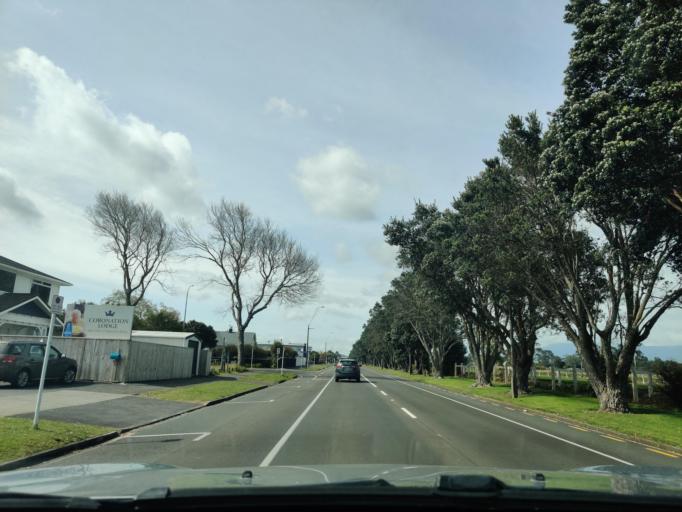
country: NZ
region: Taranaki
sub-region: New Plymouth District
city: New Plymouth
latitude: -39.0632
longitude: 174.0868
